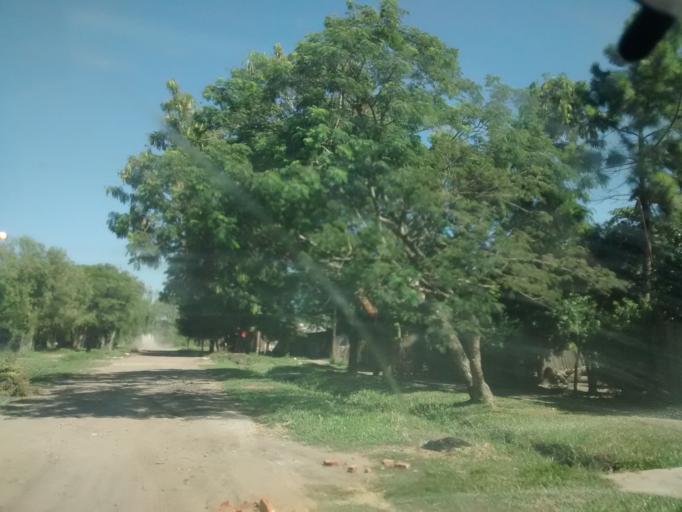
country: AR
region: Chaco
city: Fontana
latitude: -27.4091
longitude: -58.9962
